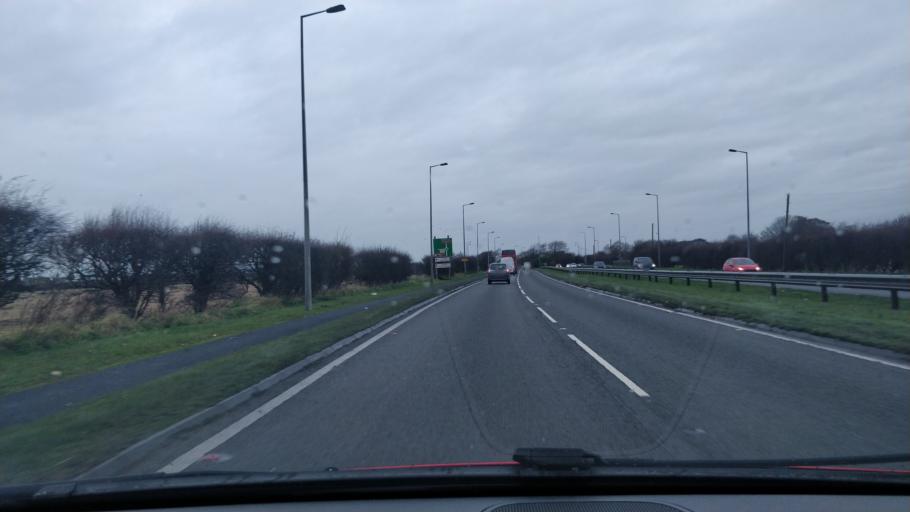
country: GB
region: England
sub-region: Sefton
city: Hightown
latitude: 53.5416
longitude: -3.0483
